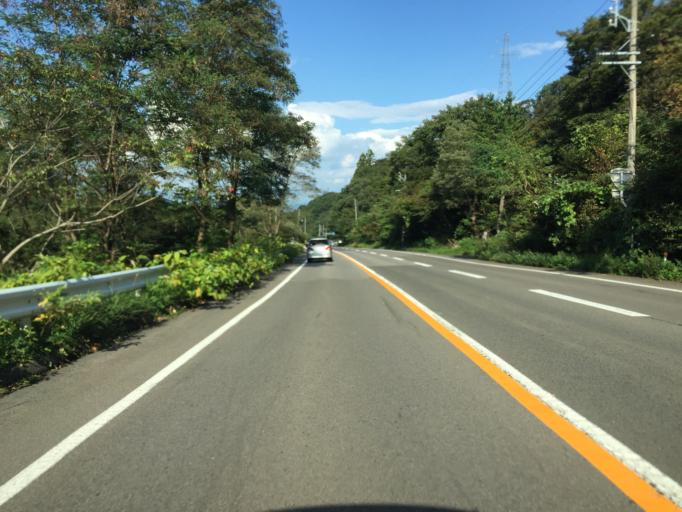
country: JP
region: Fukushima
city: Nihommatsu
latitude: 37.6897
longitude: 140.3379
